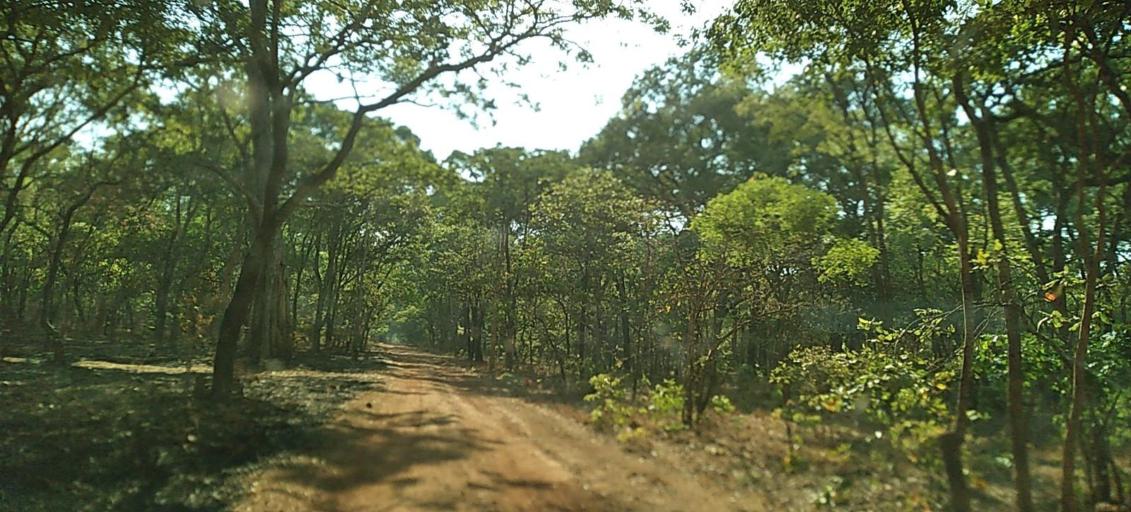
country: ZM
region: Copperbelt
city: Kalulushi
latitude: -13.0066
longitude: 27.7283
